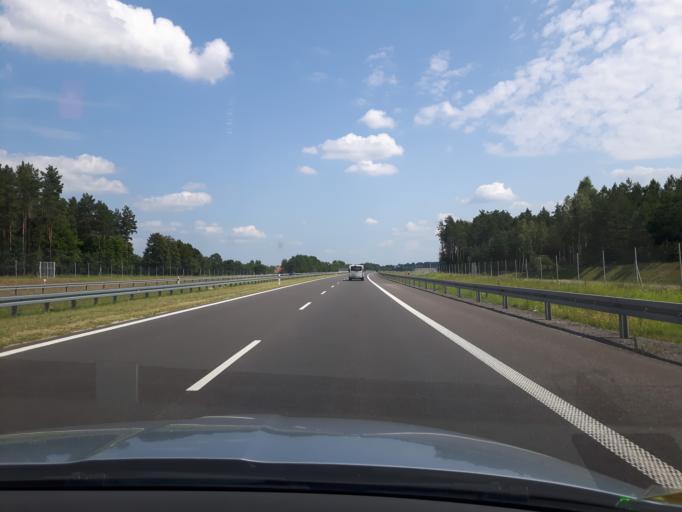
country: PL
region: Warmian-Masurian Voivodeship
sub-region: Powiat olsztynski
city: Olsztynek
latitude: 53.5873
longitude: 20.2093
